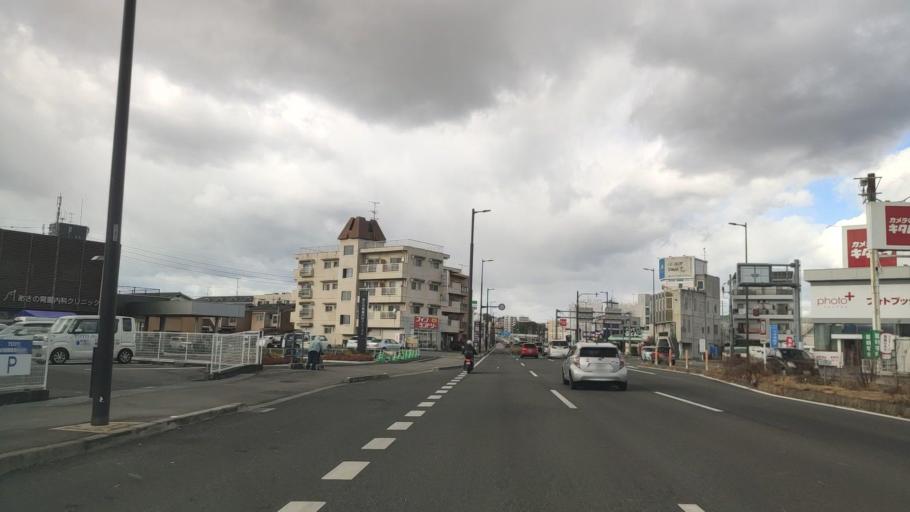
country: JP
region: Ehime
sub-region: Shikoku-chuo Shi
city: Matsuyama
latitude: 33.8302
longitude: 132.7803
